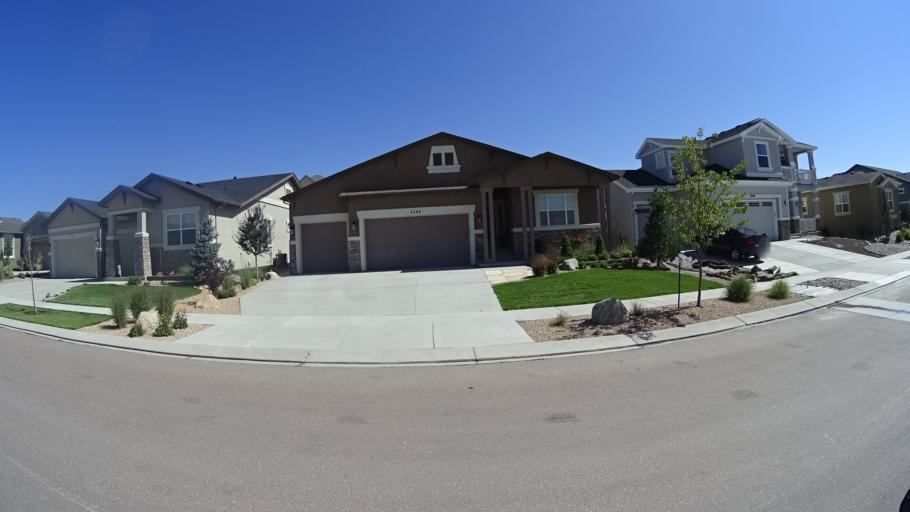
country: US
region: Colorado
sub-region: El Paso County
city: Black Forest
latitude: 38.9799
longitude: -104.7455
